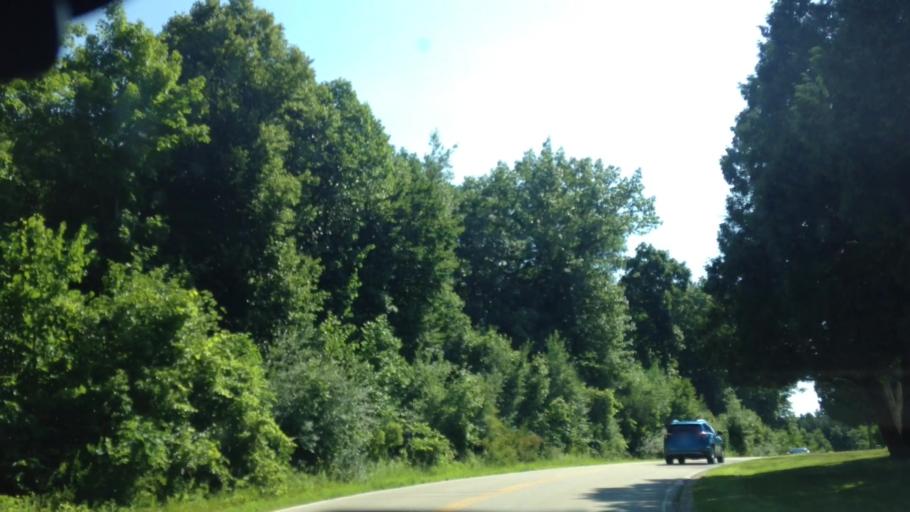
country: US
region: Wisconsin
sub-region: Washington County
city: West Bend
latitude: 43.4128
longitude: -88.2303
